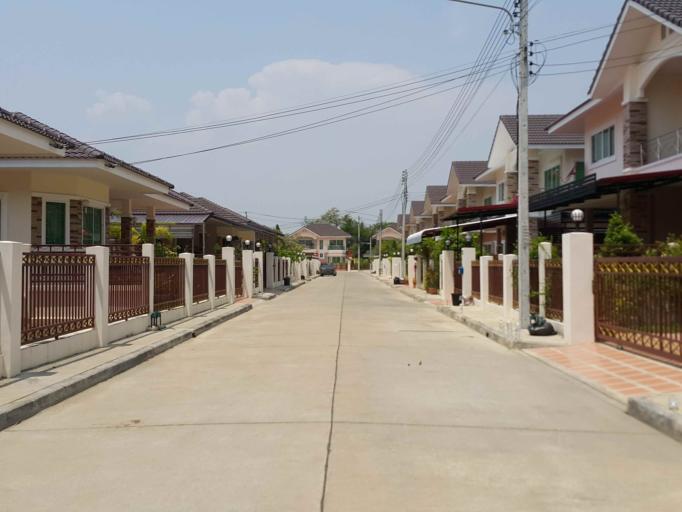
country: TH
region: Chiang Mai
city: San Kamphaeng
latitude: 18.7836
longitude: 99.0995
